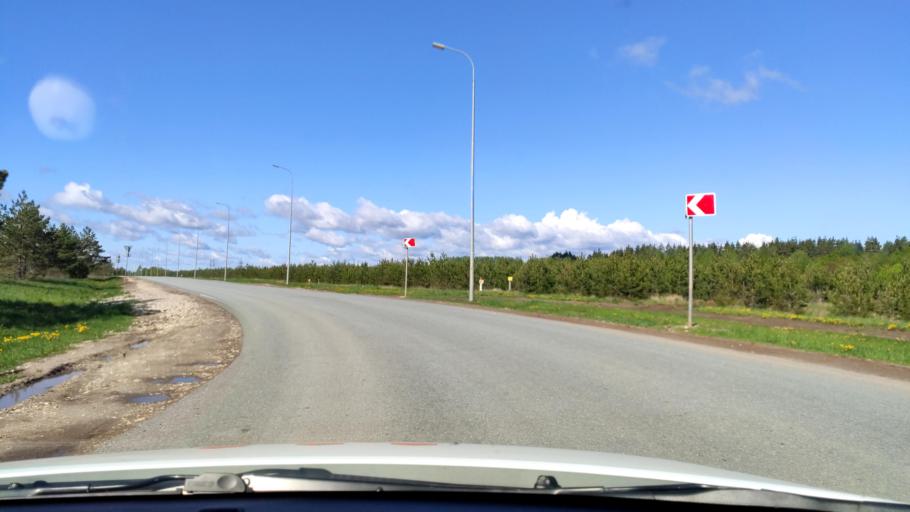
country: RU
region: Tatarstan
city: Sviyazhsk
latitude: 55.7276
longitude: 48.7590
